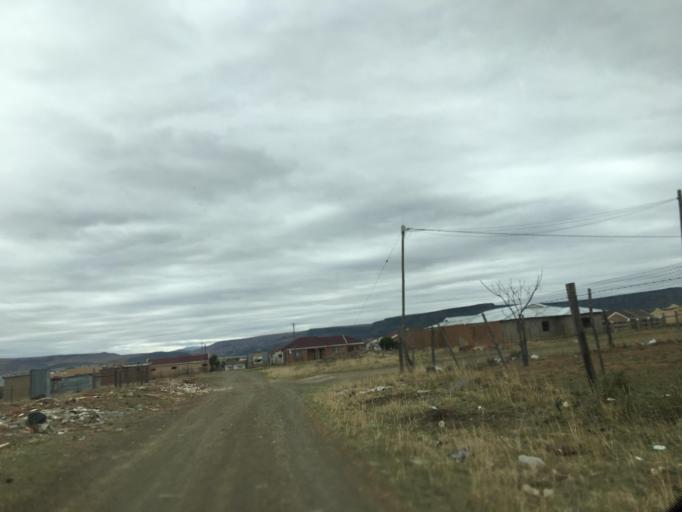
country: ZA
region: Eastern Cape
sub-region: Chris Hani District Municipality
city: Cala
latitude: -31.5401
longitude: 27.6963
